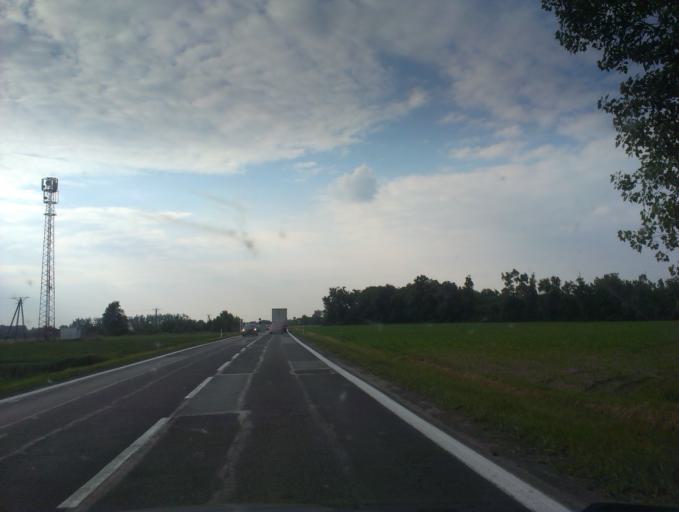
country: PL
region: Lower Silesian Voivodeship
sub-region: Powiat trzebnicki
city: Prusice
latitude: 51.3716
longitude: 16.9521
